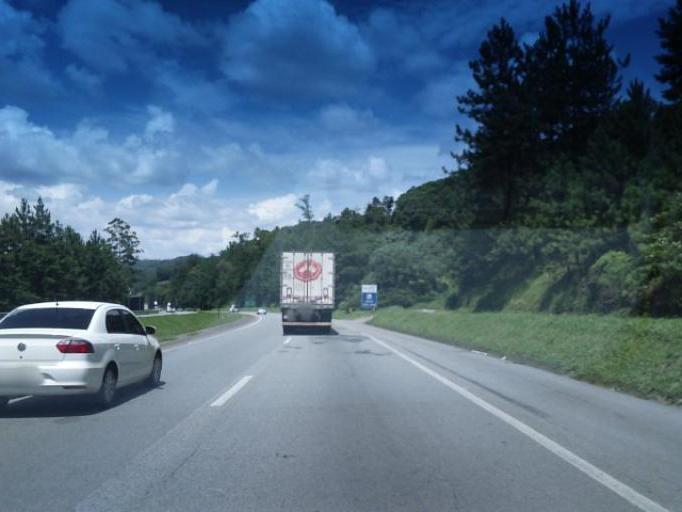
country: BR
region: Sao Paulo
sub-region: Juquitiba
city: Juquitiba
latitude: -23.9382
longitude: -47.0852
